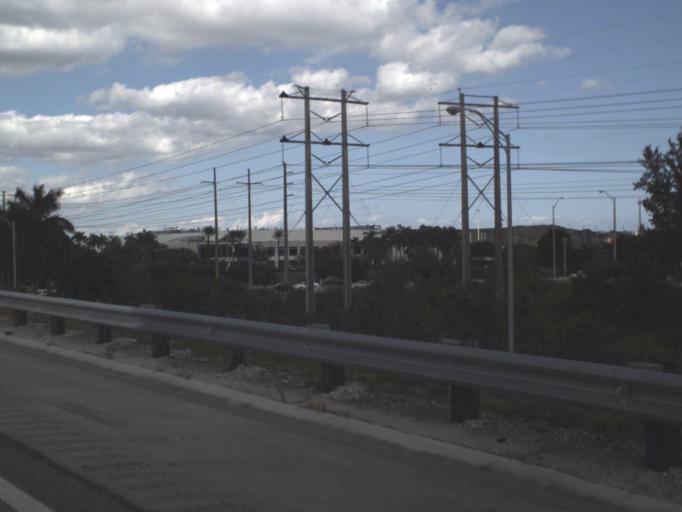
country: US
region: Florida
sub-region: Broward County
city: Davie
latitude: 26.0642
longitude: -80.2152
